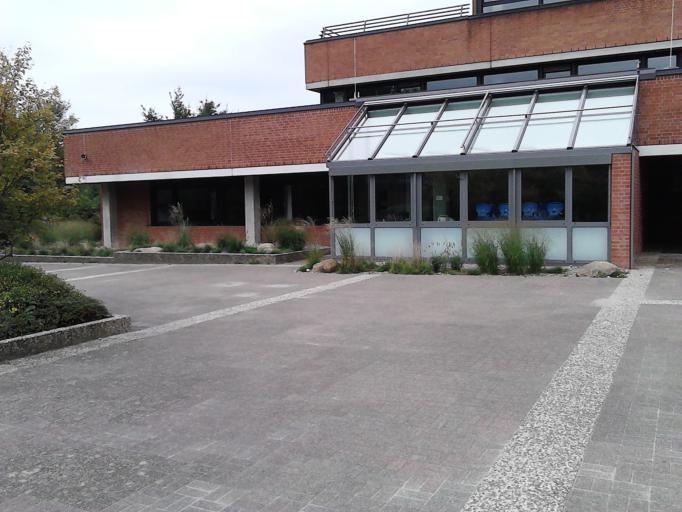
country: DE
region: Lower Saxony
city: Lueneburg
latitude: 53.2454
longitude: 10.4303
